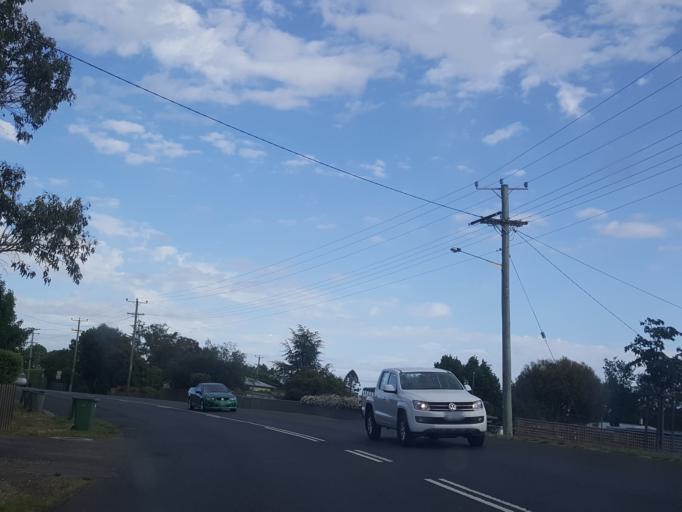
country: AU
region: Tasmania
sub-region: Northern Midlands
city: Perth
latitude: -41.5800
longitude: 147.1787
